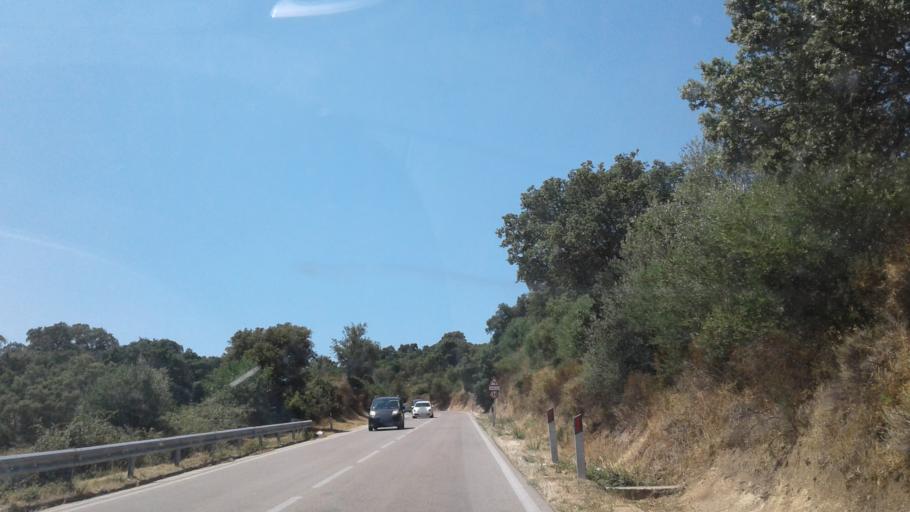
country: IT
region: Sardinia
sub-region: Provincia di Olbia-Tempio
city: Luras
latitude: 40.9528
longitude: 9.2033
